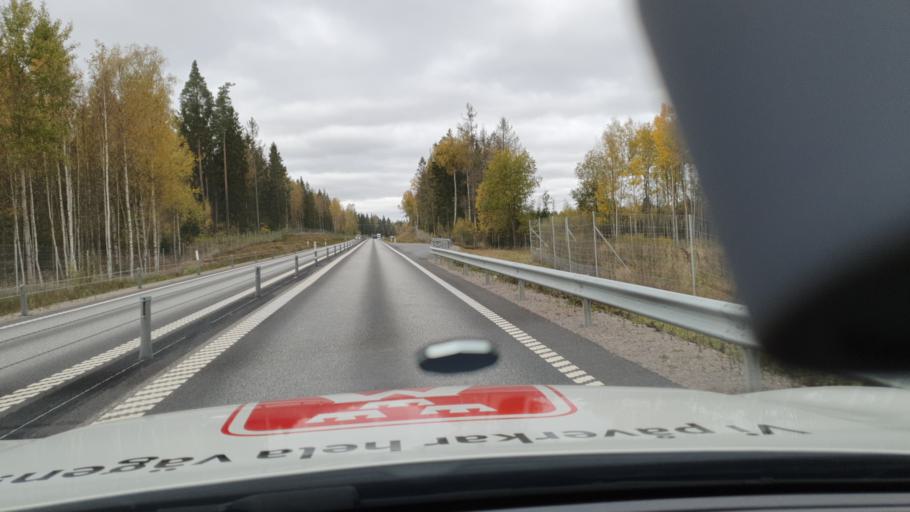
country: SE
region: OErebro
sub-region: Hallsbergs Kommun
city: Skollersta
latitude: 59.1175
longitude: 15.2972
